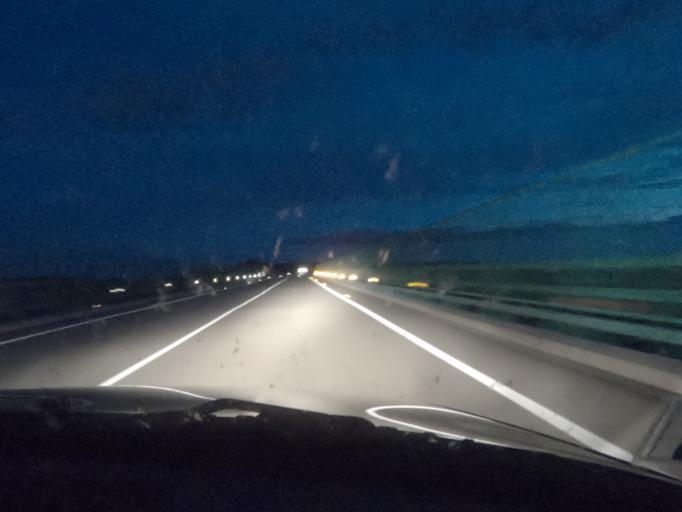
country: ES
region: Extremadura
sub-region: Provincia de Caceres
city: Carcaboso
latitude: 39.9813
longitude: -6.1613
